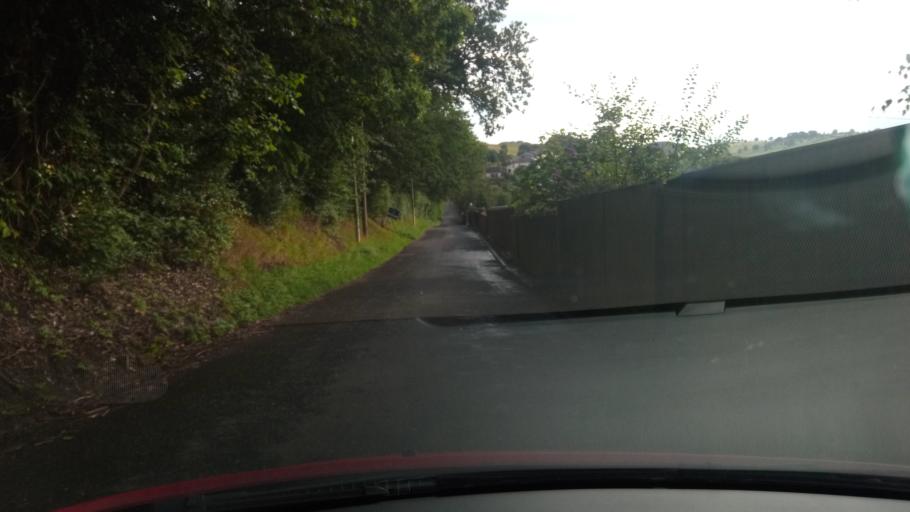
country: GB
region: Scotland
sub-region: The Scottish Borders
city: Hawick
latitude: 55.4221
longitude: -2.7788
